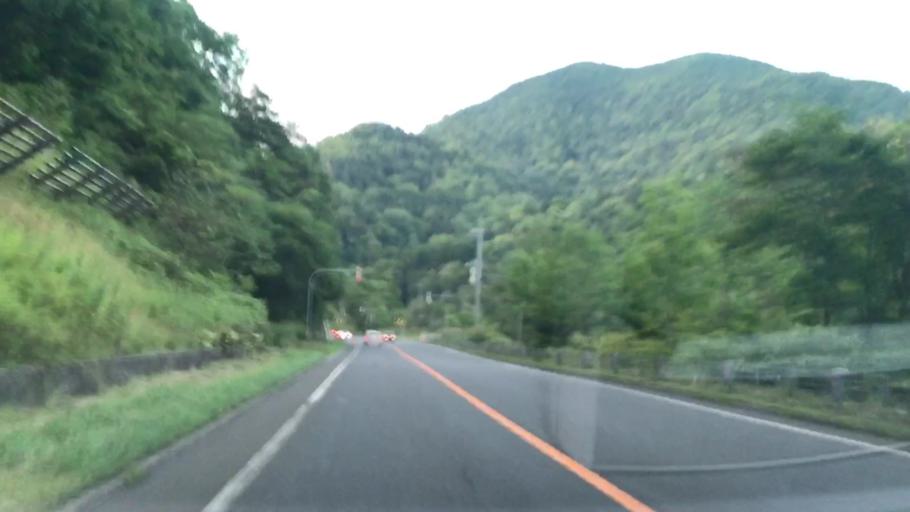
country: JP
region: Hokkaido
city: Sapporo
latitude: 42.9183
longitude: 141.1249
